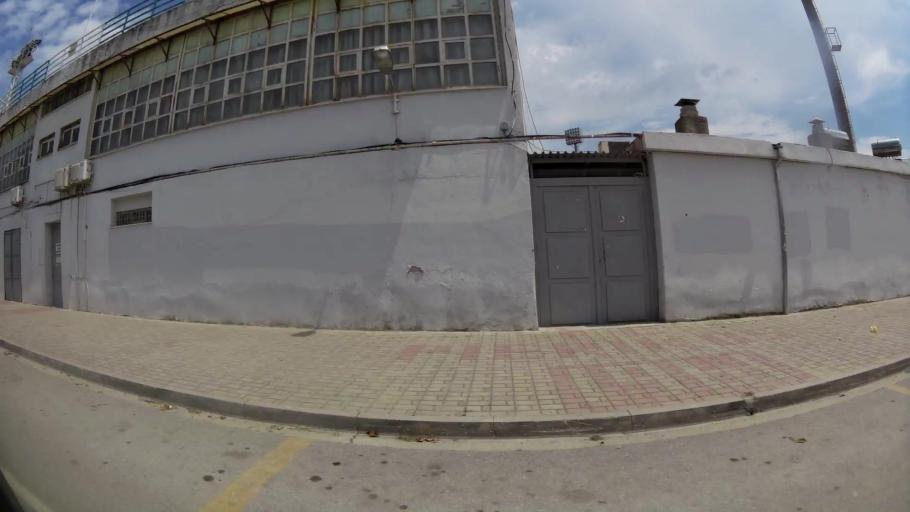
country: GR
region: Central Macedonia
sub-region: Nomos Pierias
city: Katerini
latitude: 40.2608
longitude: 22.5117
